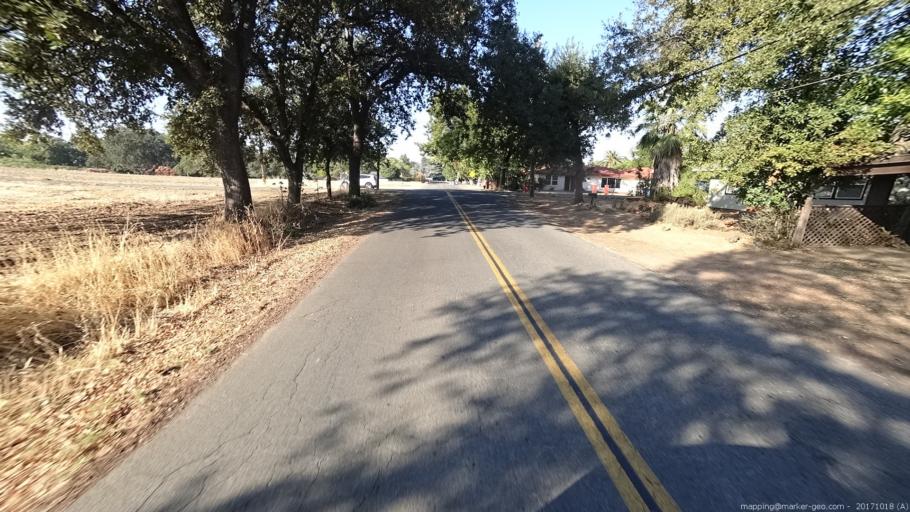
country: US
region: California
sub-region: Shasta County
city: Redding
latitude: 40.5615
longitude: -122.3699
